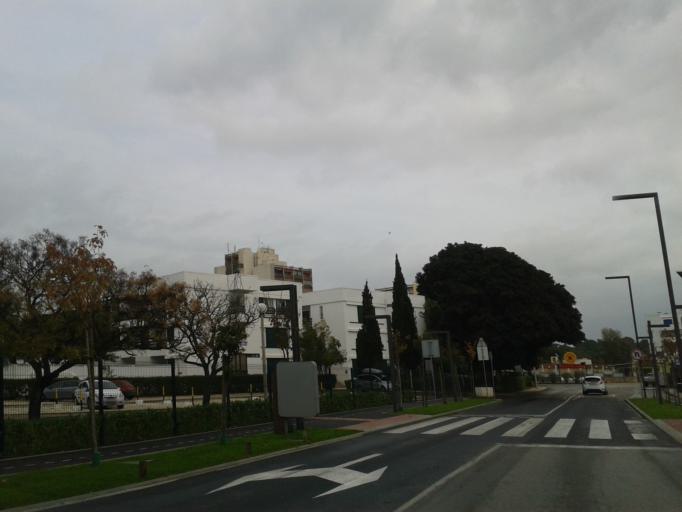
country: PT
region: Faro
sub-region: Loule
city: Vilamoura
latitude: 37.0784
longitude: -8.1154
